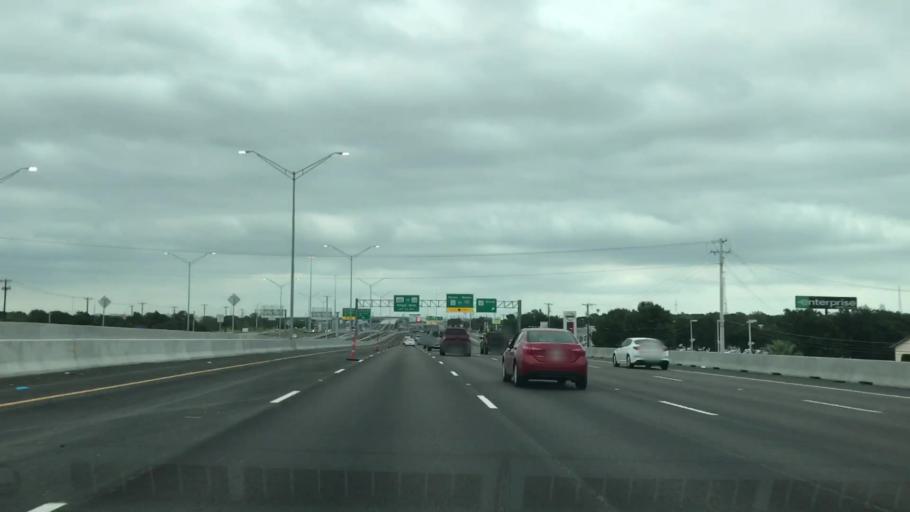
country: US
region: Texas
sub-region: Dallas County
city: Irving
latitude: 32.8368
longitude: -96.9295
